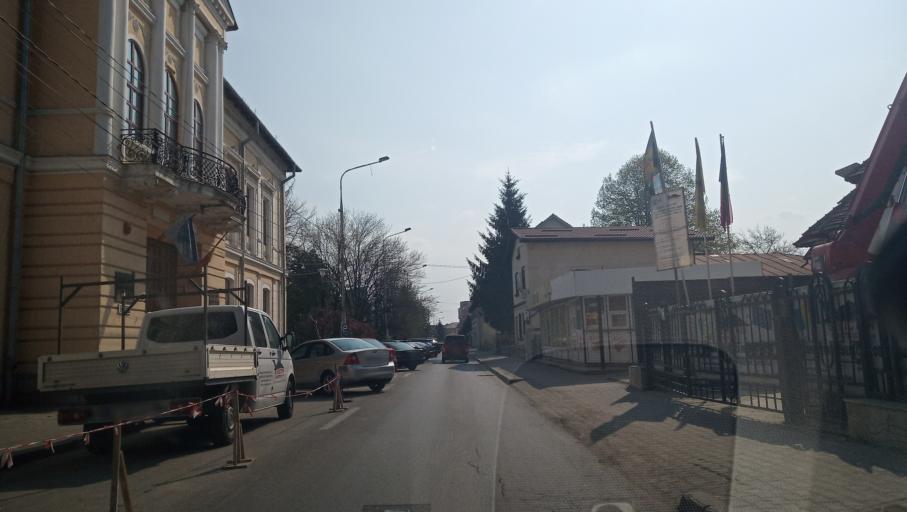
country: RO
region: Gorj
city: Targu Jiu
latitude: 45.0396
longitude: 23.2761
